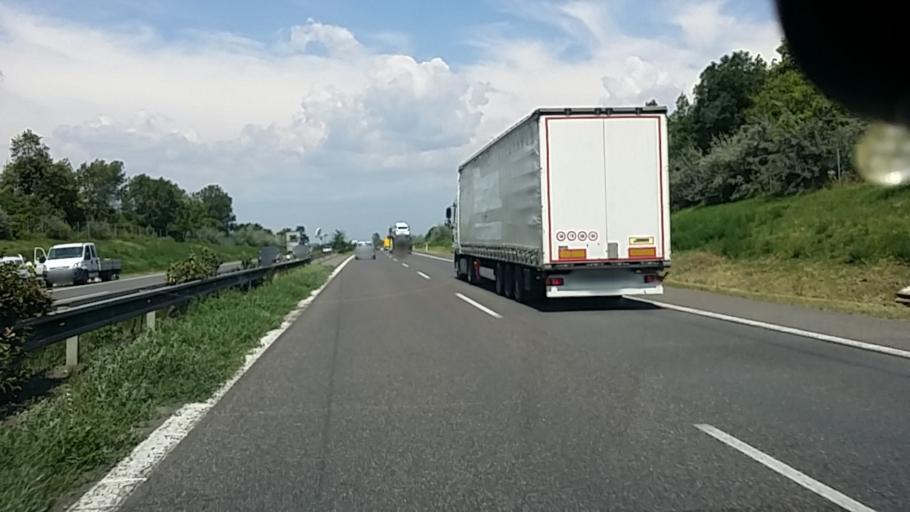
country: SK
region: Bratislavsky
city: Stupava
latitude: 48.2742
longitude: 17.0088
